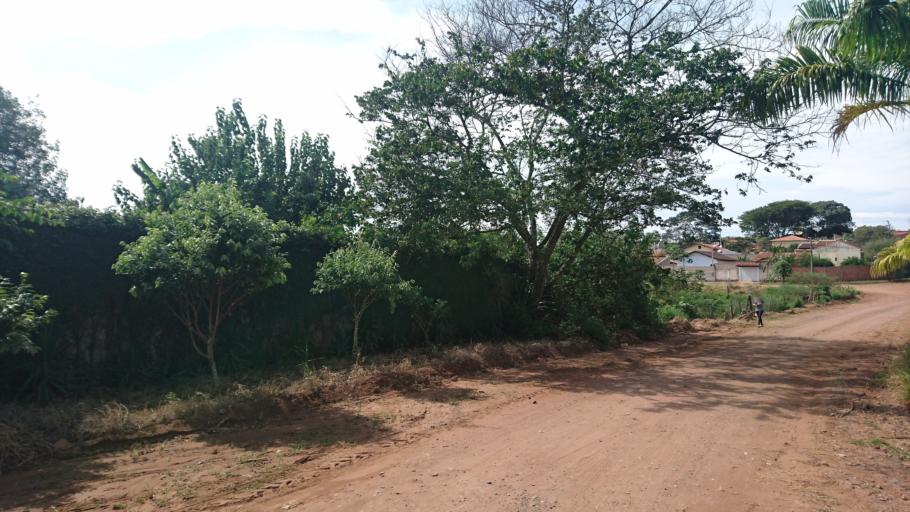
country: BR
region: Sao Paulo
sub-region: Casa Branca
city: Casa Branca
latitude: -21.7831
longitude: -47.0923
